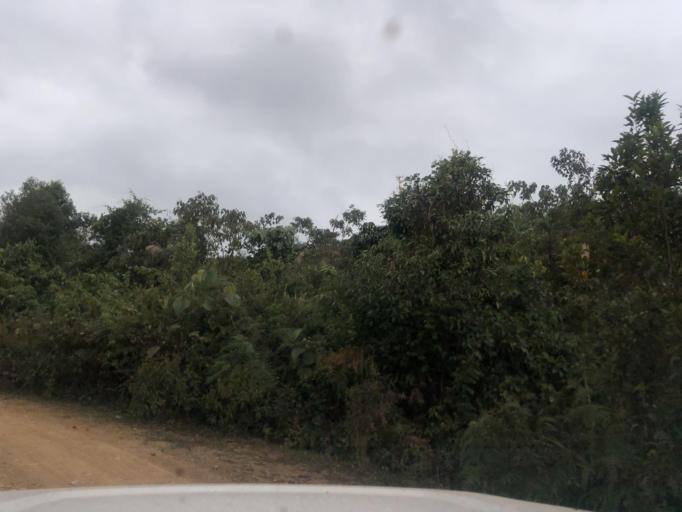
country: LA
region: Phongsali
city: Khoa
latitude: 21.2615
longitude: 102.5891
